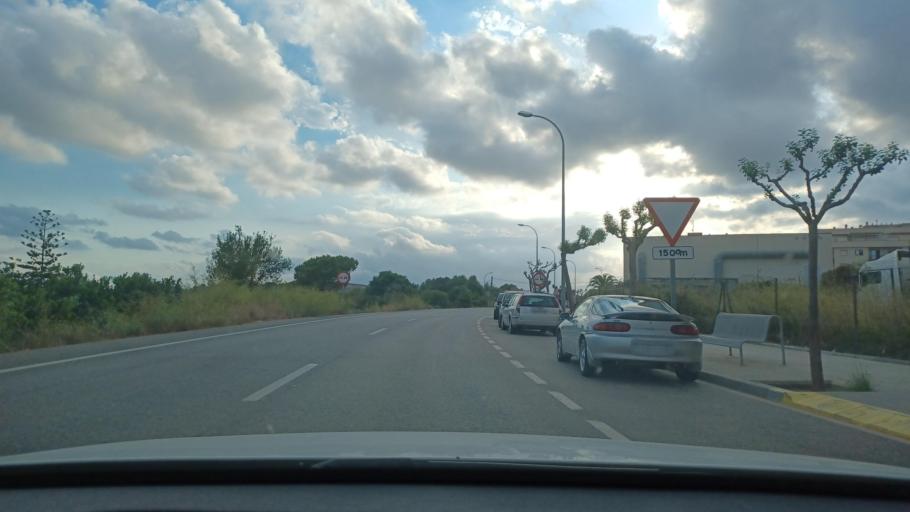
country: ES
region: Catalonia
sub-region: Provincia de Tarragona
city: Alcanar
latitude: 40.5398
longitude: 0.4835
